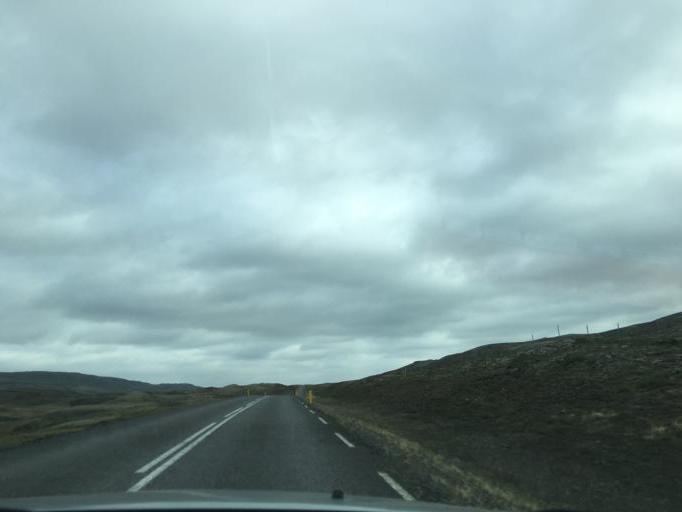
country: IS
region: South
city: Vestmannaeyjar
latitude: 64.2606
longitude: -20.1968
